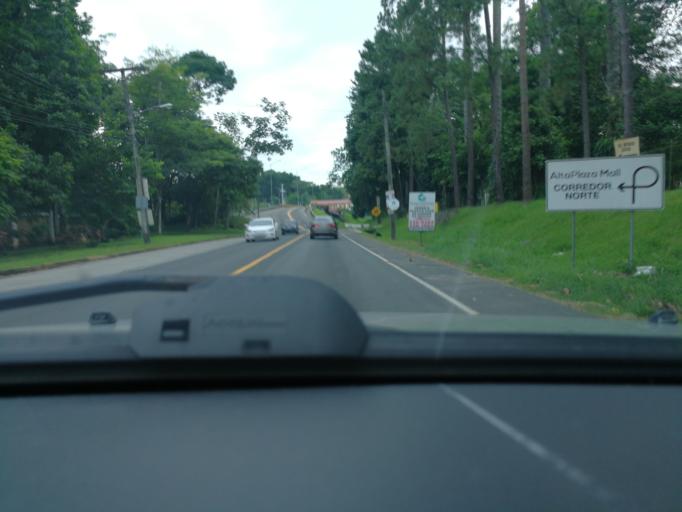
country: PA
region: Panama
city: Panama
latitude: 9.0091
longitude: -79.5438
